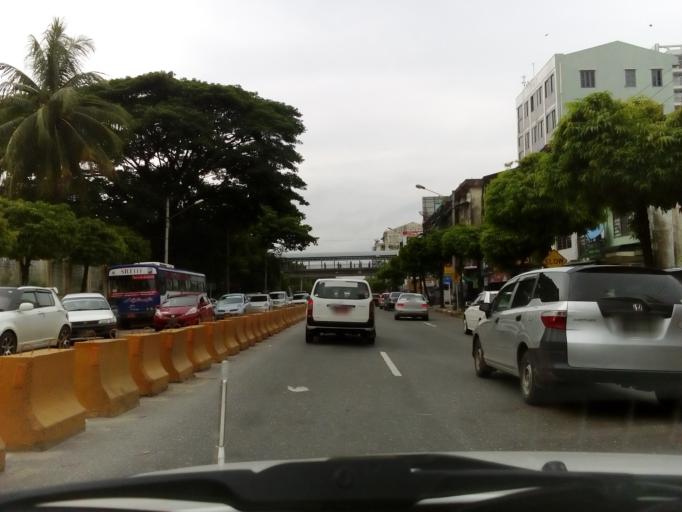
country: MM
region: Yangon
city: Yangon
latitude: 16.8549
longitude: 96.1571
